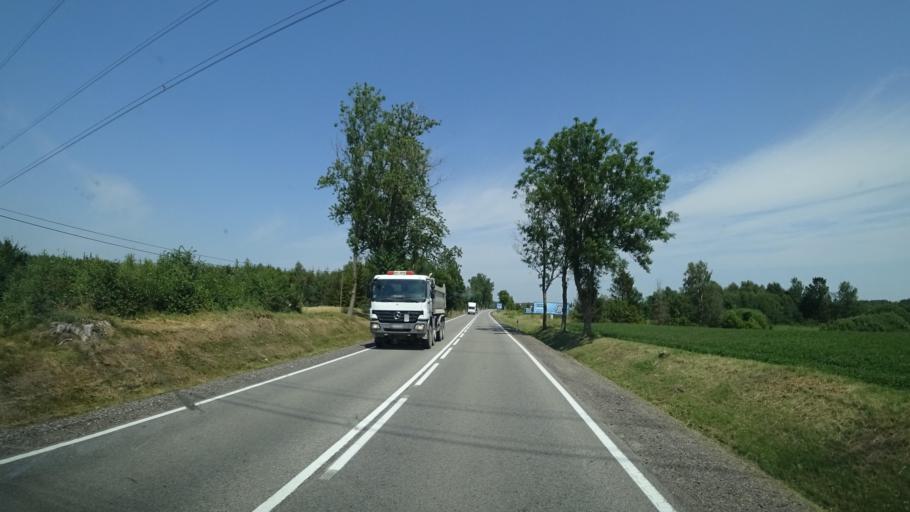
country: PL
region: Pomeranian Voivodeship
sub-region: Powiat koscierski
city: Koscierzyna
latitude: 54.1554
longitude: 18.0323
